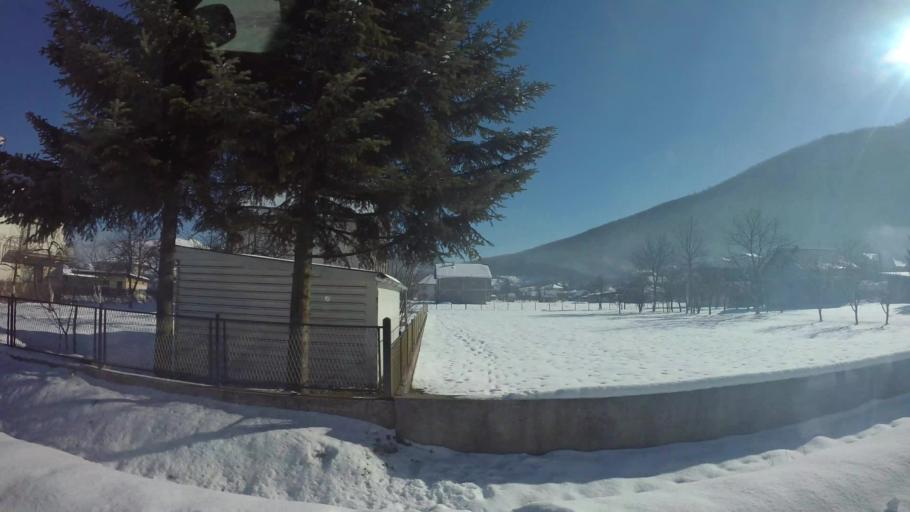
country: BA
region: Federation of Bosnia and Herzegovina
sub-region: Kanton Sarajevo
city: Sarajevo
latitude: 43.7897
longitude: 18.3378
